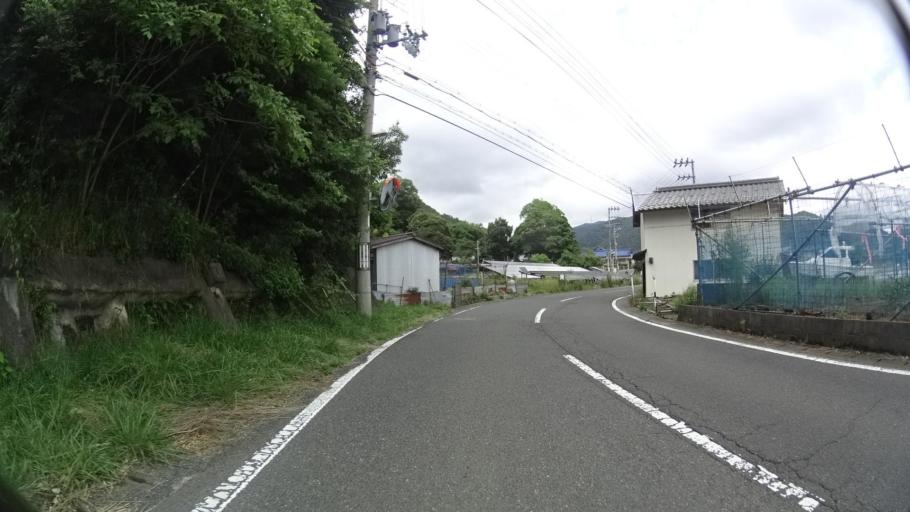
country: JP
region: Kyoto
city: Maizuru
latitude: 35.5132
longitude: 135.3859
